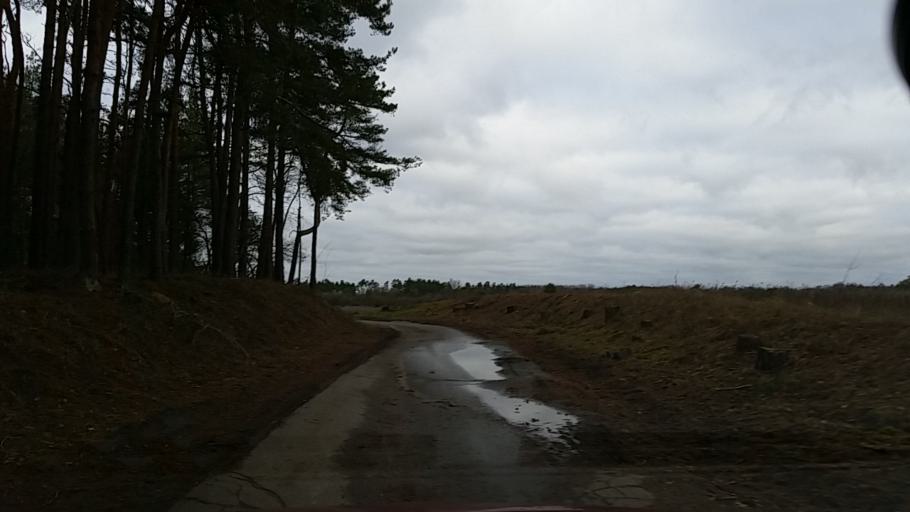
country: DE
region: Lower Saxony
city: Wieren
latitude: 52.8639
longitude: 10.6579
